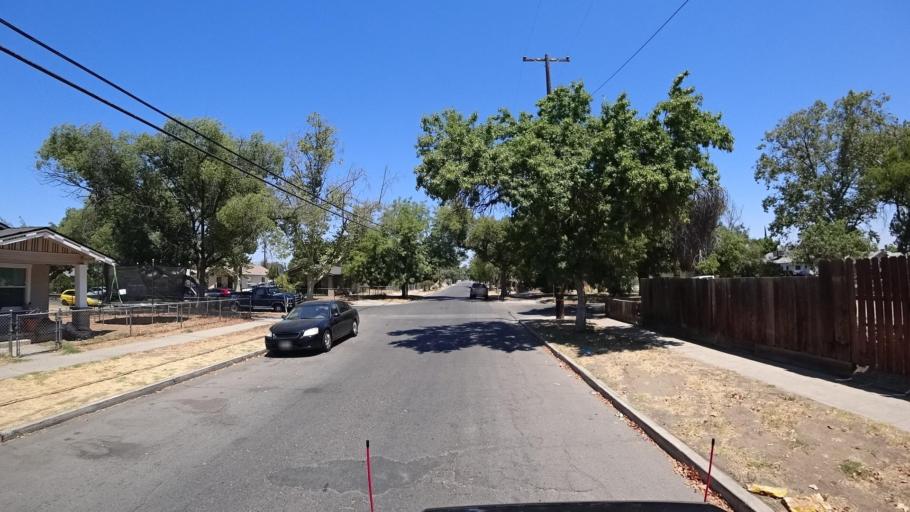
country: US
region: California
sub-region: Fresno County
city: Fresno
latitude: 36.7593
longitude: -119.7838
